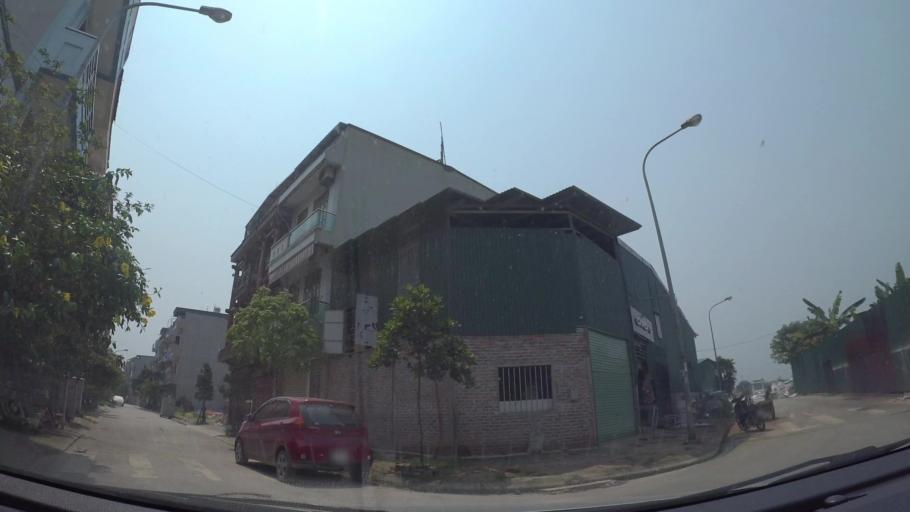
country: VN
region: Ha Noi
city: Ha Dong
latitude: 20.9854
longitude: 105.7719
